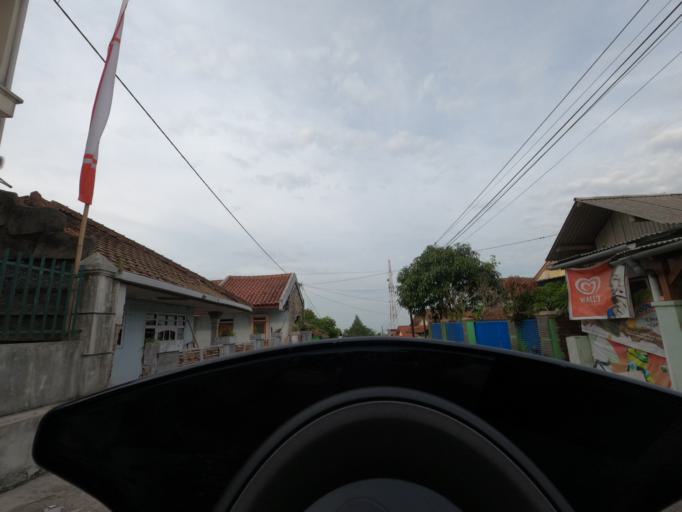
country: ID
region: West Java
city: Lembang
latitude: -6.7331
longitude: 107.6467
